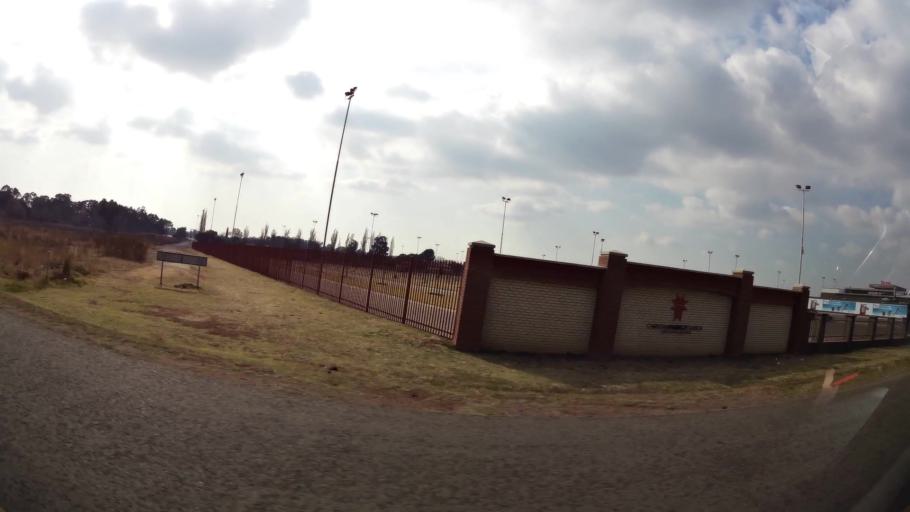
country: ZA
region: Gauteng
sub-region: Ekurhuleni Metropolitan Municipality
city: Benoni
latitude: -26.1317
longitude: 28.2665
